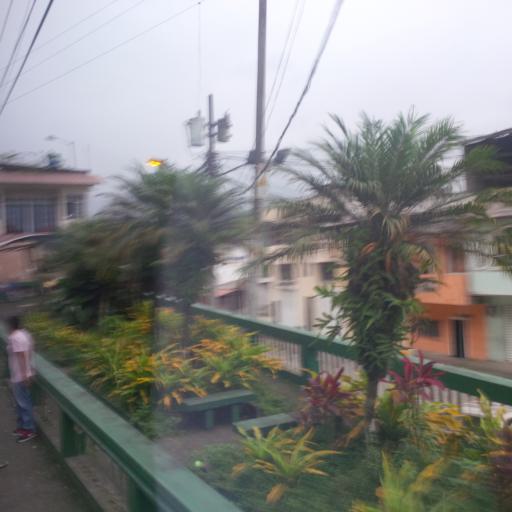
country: EC
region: Chimborazo
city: Alausi
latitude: -2.2020
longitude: -79.1308
